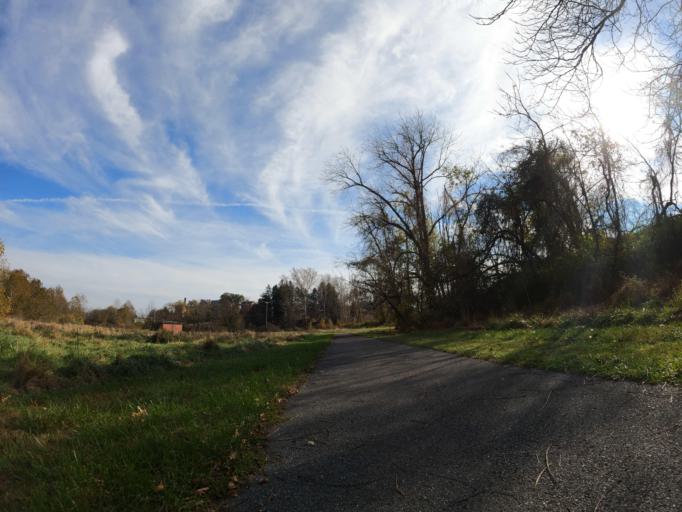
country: US
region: Maryland
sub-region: Carroll County
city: Sykesville
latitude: 39.3811
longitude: -76.9638
